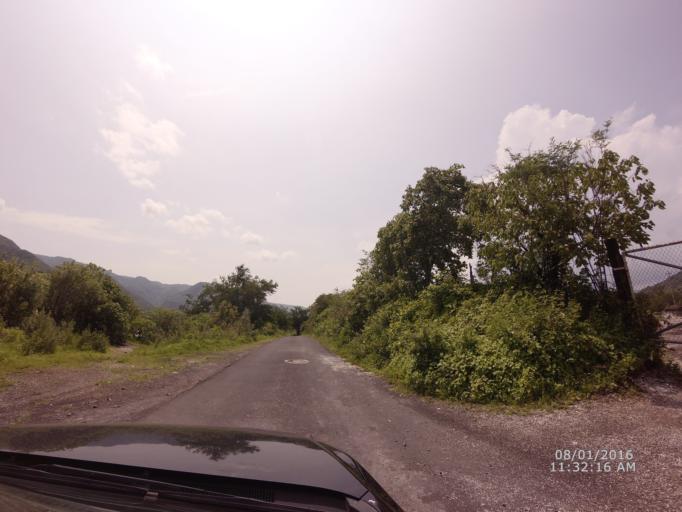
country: MX
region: Nayarit
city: Jala
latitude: 21.1070
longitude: -104.4483
